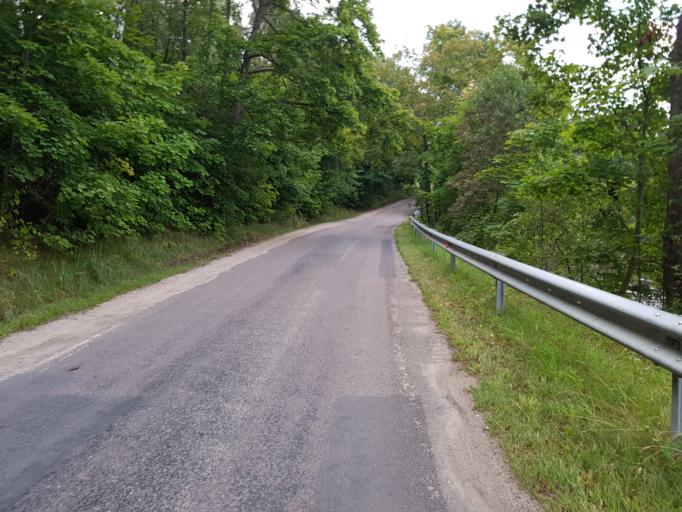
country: LT
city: Trakai
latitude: 54.6711
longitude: 24.9357
